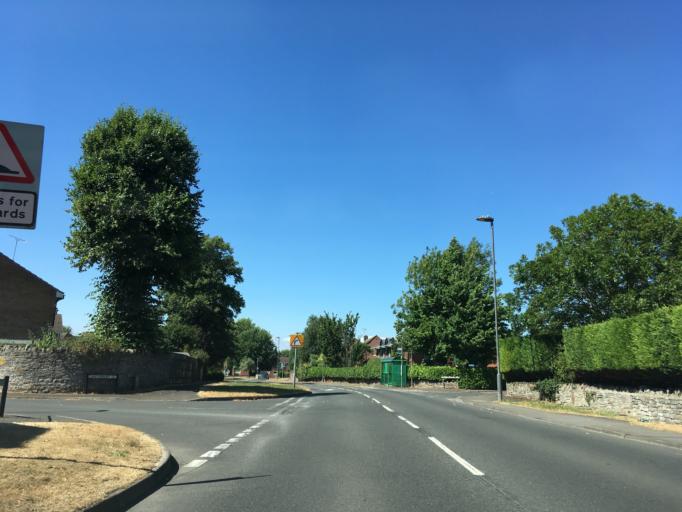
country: GB
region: England
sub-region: South Gloucestershire
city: Yate
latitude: 51.5456
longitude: -2.4115
